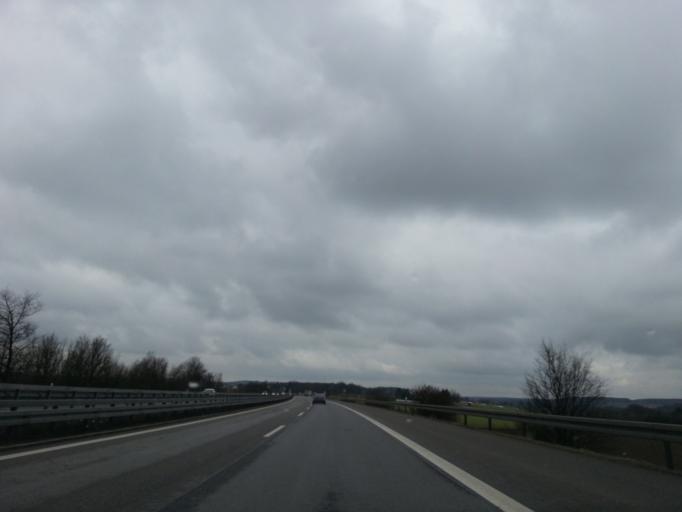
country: DE
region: Bavaria
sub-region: Upper Palatinate
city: Deuerling
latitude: 49.0527
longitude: 11.9270
